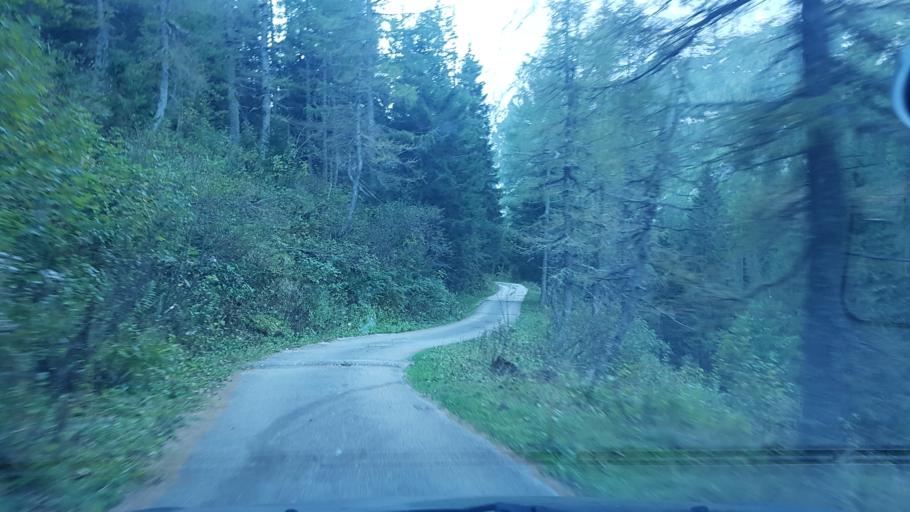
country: IT
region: Veneto
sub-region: Provincia di Belluno
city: Fusine
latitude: 46.3586
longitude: 12.0913
